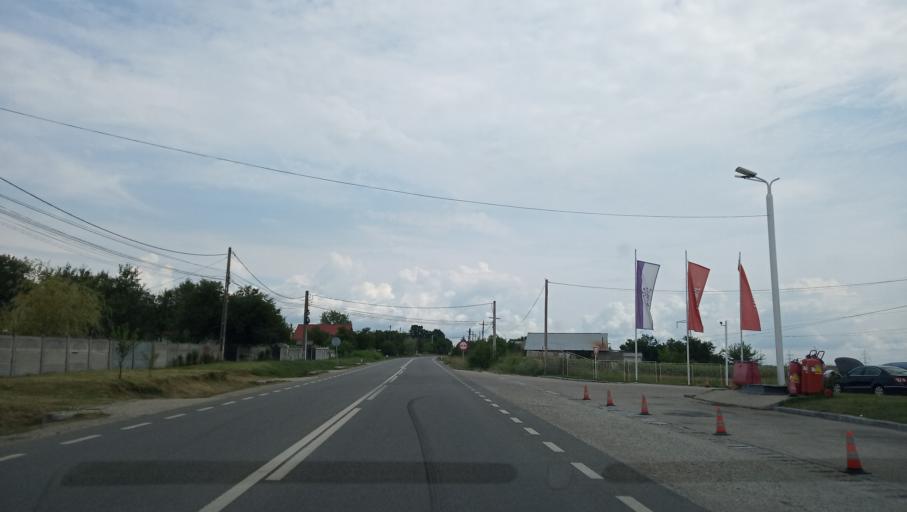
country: RO
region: Gorj
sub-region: Comuna Branesti
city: Branesti
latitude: 44.6809
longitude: 23.4230
